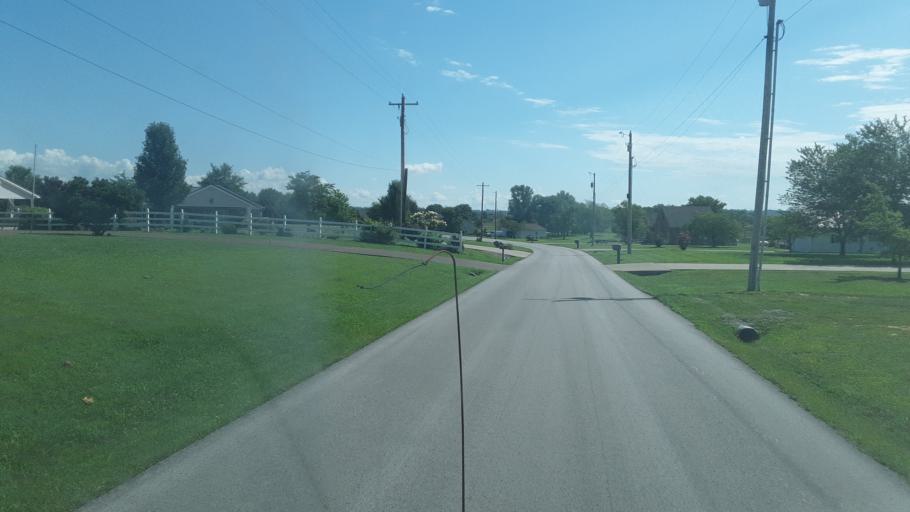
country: US
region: Kentucky
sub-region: Todd County
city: Elkton
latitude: 36.8117
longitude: -87.1793
